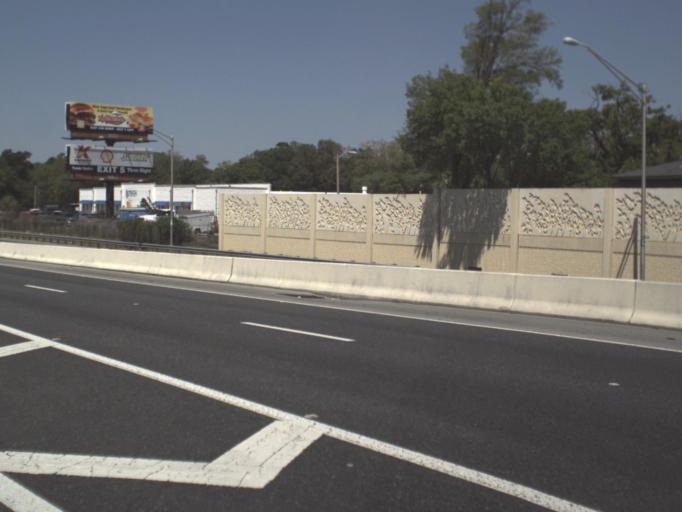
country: US
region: Florida
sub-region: Escambia County
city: Ferry Pass
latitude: 30.5038
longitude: -87.2246
